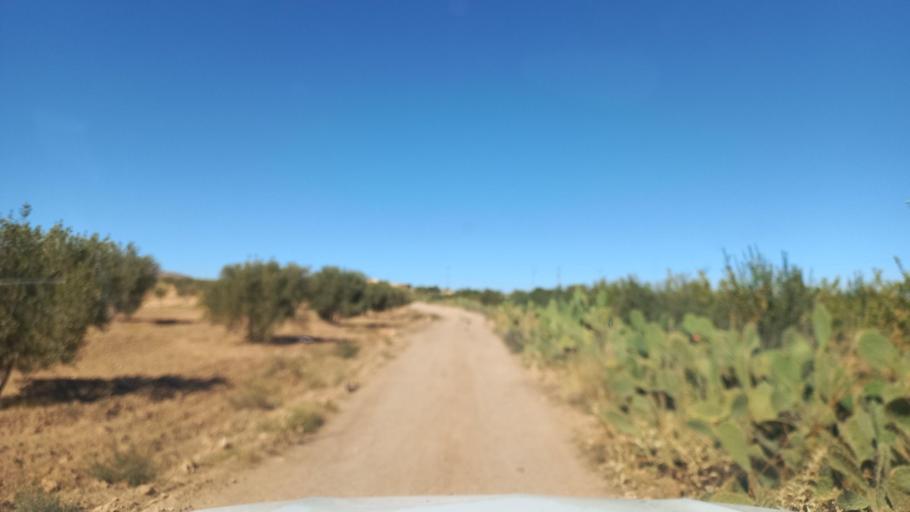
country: TN
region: Al Qasrayn
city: Sbiba
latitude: 35.3966
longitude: 9.0838
